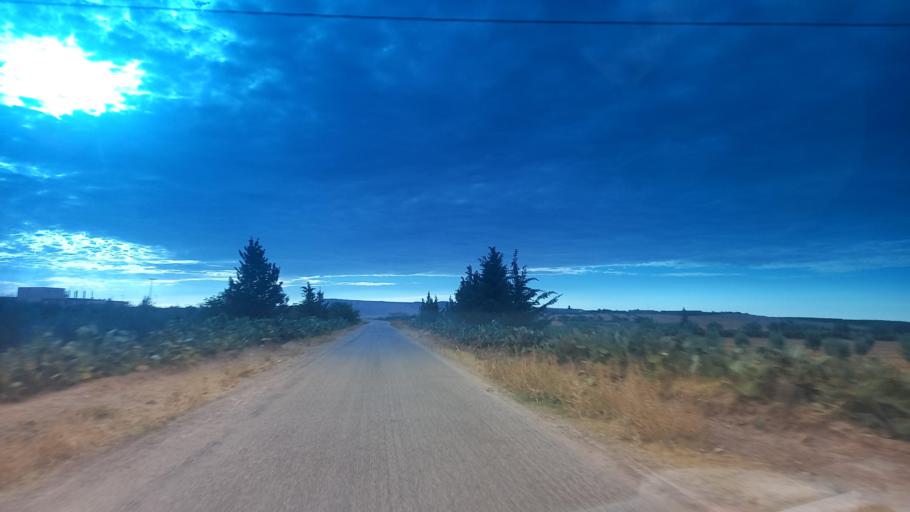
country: TN
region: Al Qasrayn
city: Sbiba
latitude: 35.3841
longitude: 9.0389
